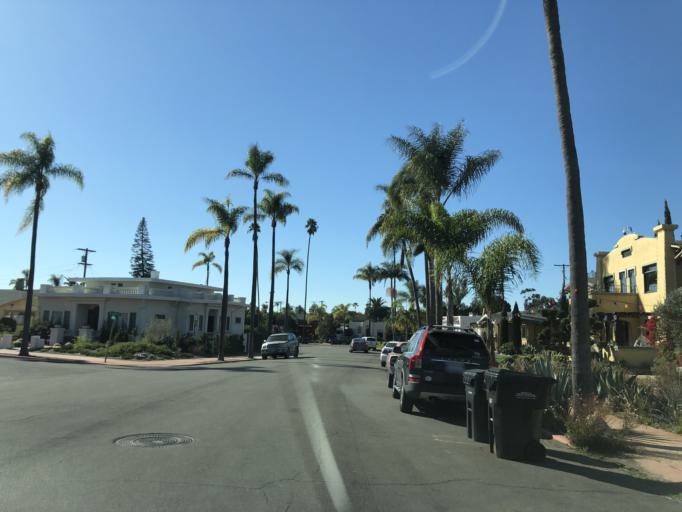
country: US
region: California
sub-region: San Diego County
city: San Diego
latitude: 32.7324
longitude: -117.1276
